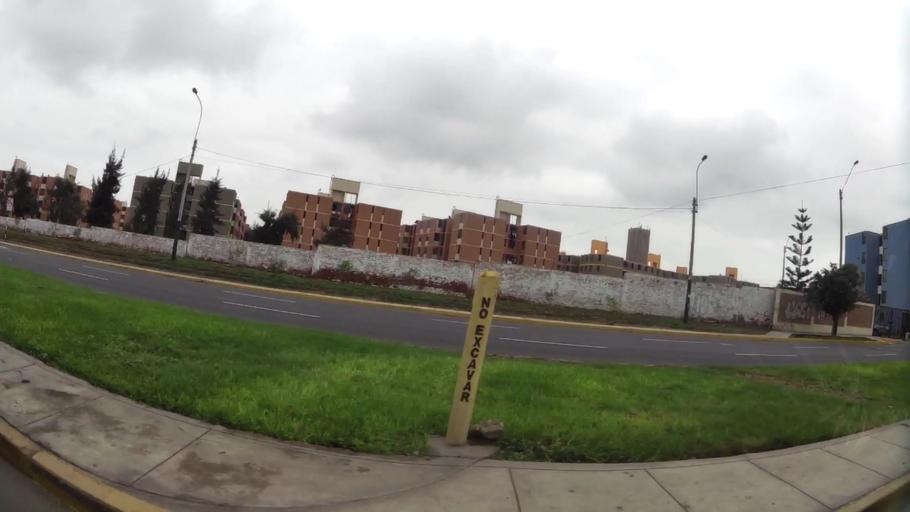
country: PE
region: Lima
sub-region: Lima
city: Surco
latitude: -12.1552
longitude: -76.9907
